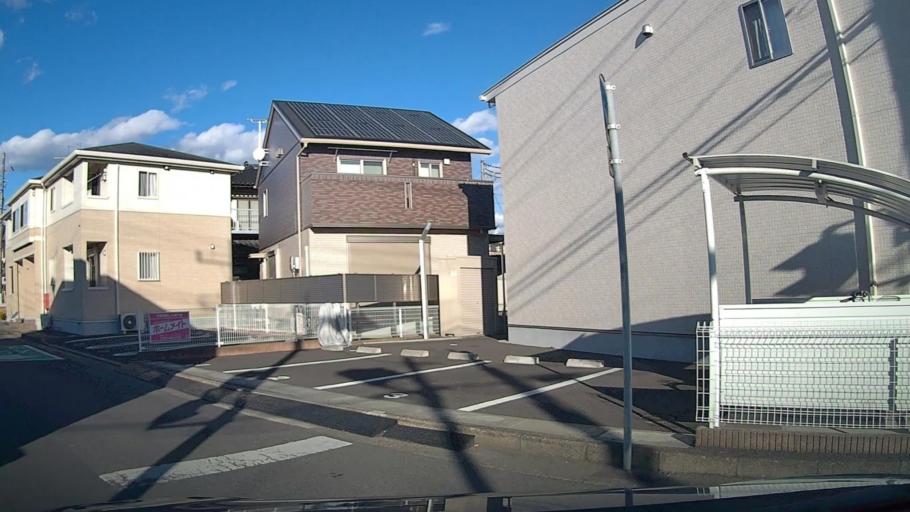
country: JP
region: Ibaraki
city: Mito-shi
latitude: 36.3847
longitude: 140.4510
